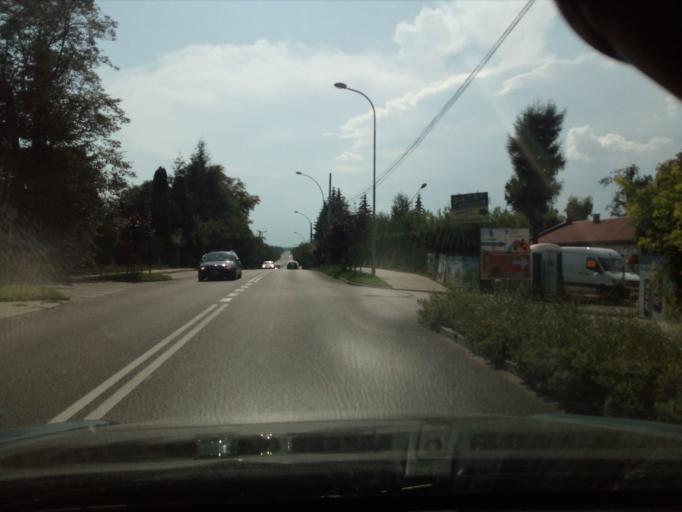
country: PL
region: Subcarpathian Voivodeship
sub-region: Powiat lancucki
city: Lancut
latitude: 50.0633
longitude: 22.2216
